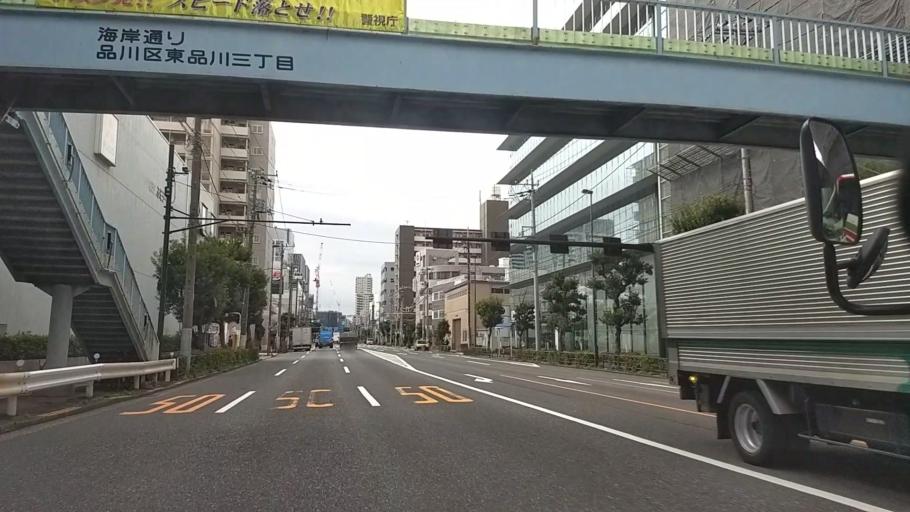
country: JP
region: Tokyo
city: Tokyo
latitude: 35.6154
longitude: 139.7479
